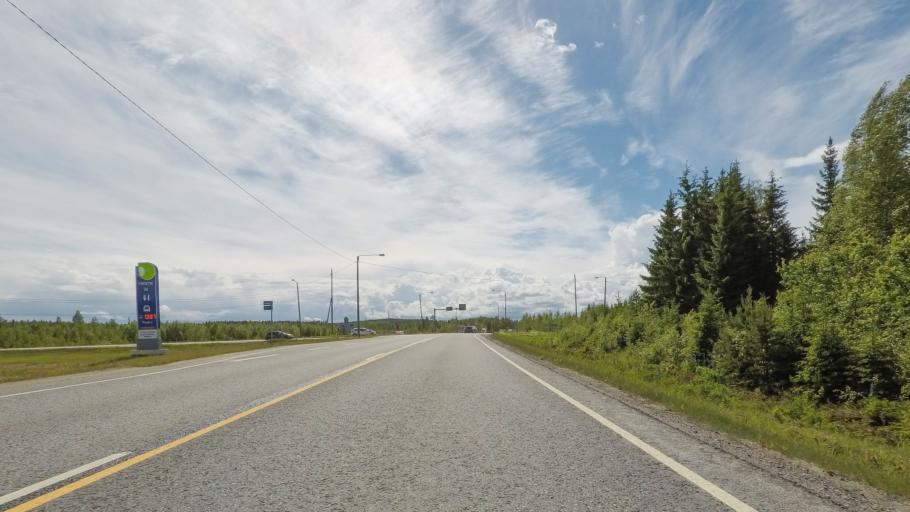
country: FI
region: Central Finland
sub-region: Jyvaeskylae
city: Hankasalmi
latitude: 62.3582
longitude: 26.5701
